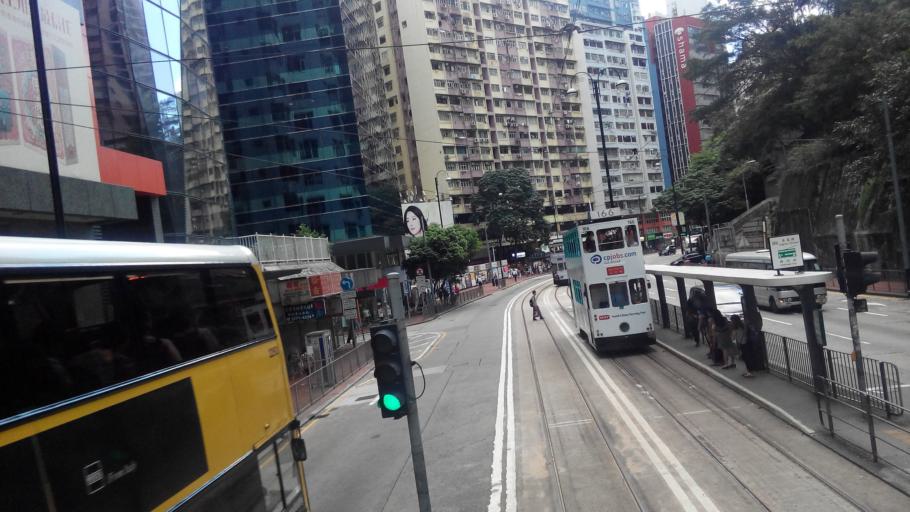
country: HK
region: Wanchai
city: Wan Chai
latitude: 22.2866
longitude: 114.1930
